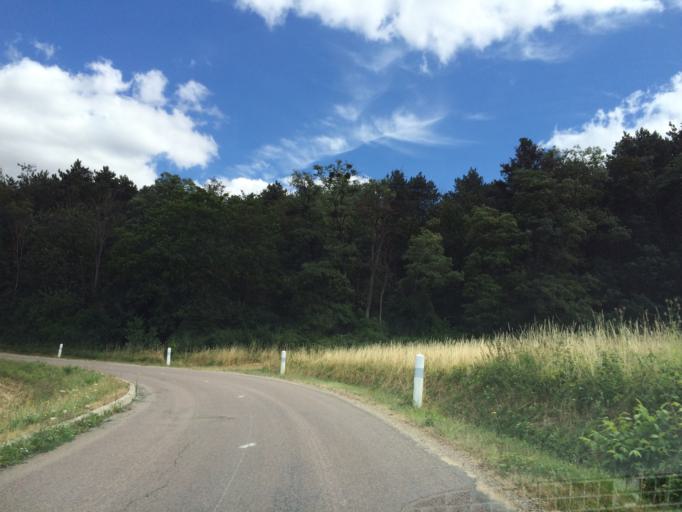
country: FR
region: Bourgogne
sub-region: Departement de l'Yonne
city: Fleury-la-Vallee
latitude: 47.8702
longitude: 3.4638
